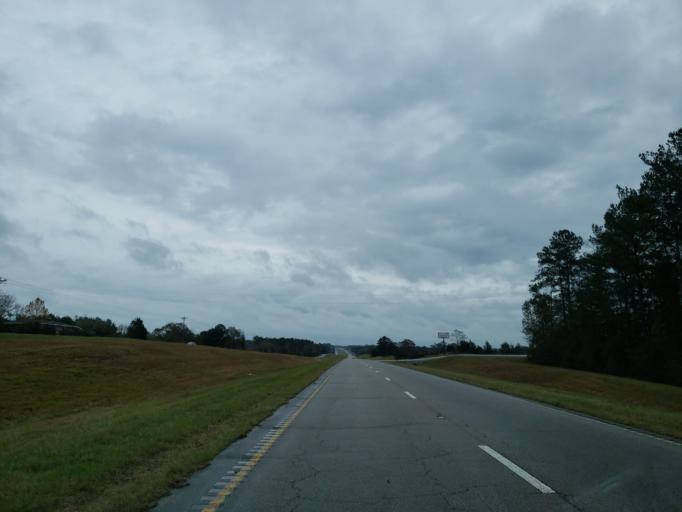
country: US
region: Mississippi
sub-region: Wayne County
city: Waynesboro
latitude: 31.6966
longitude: -88.8645
